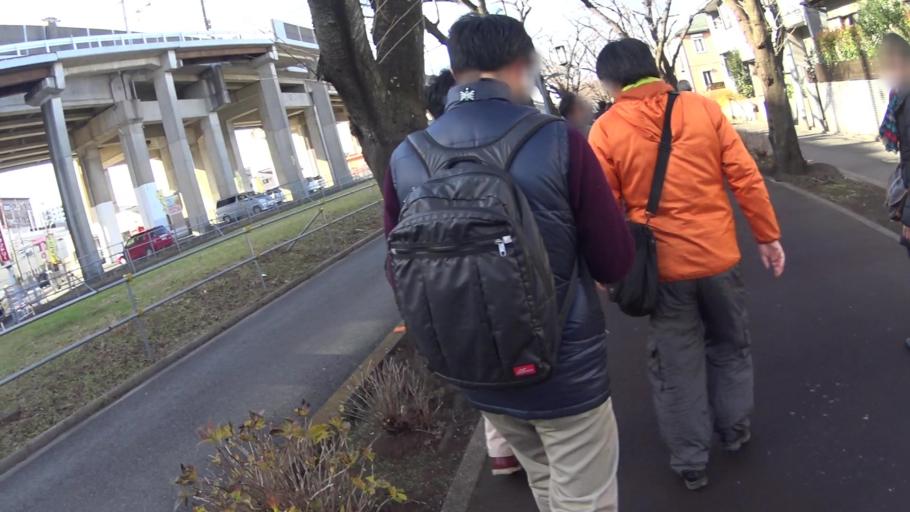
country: JP
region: Saitama
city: Yono
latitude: 35.8496
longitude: 139.6438
